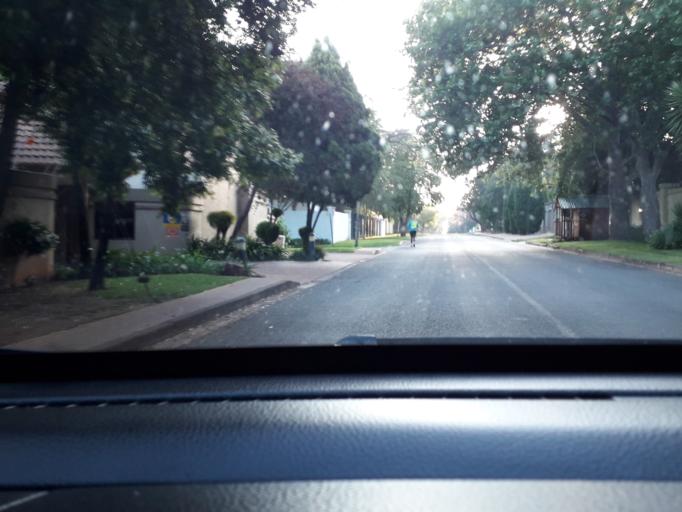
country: ZA
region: Gauteng
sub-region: City of Johannesburg Metropolitan Municipality
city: Johannesburg
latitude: -26.1602
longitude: 28.0509
